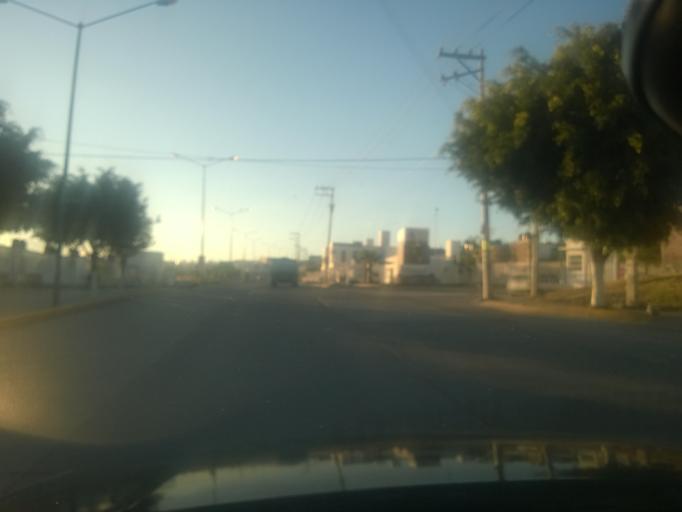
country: MX
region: Guanajuato
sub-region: Leon
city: La Ermita
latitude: 21.1561
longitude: -101.7396
